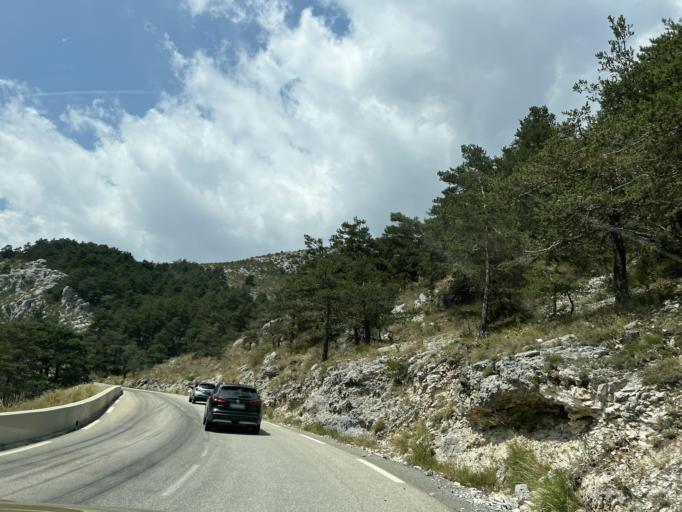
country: FR
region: Provence-Alpes-Cote d'Azur
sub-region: Departement des Alpes-Maritimes
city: Saint-Vallier-de-Thiey
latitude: 43.8013
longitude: 6.9079
